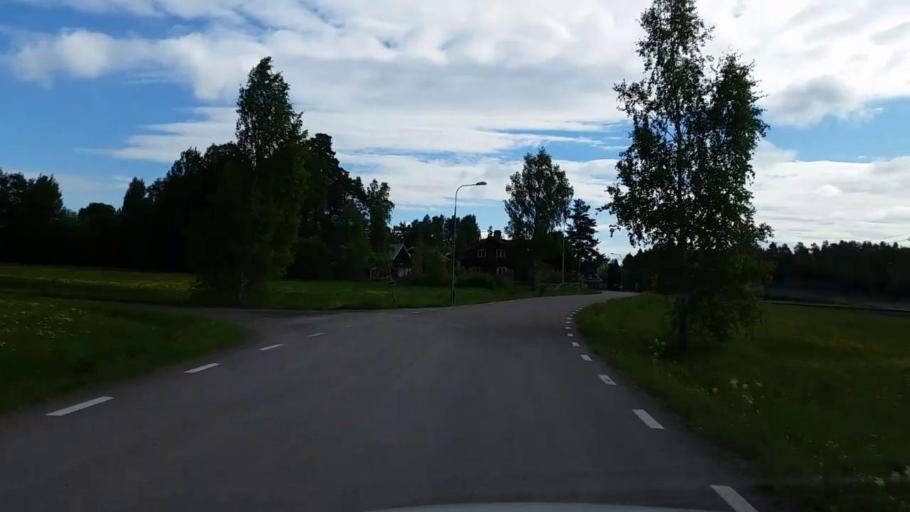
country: SE
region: Dalarna
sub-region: Borlange Kommun
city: Ornas
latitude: 60.5089
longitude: 15.5925
